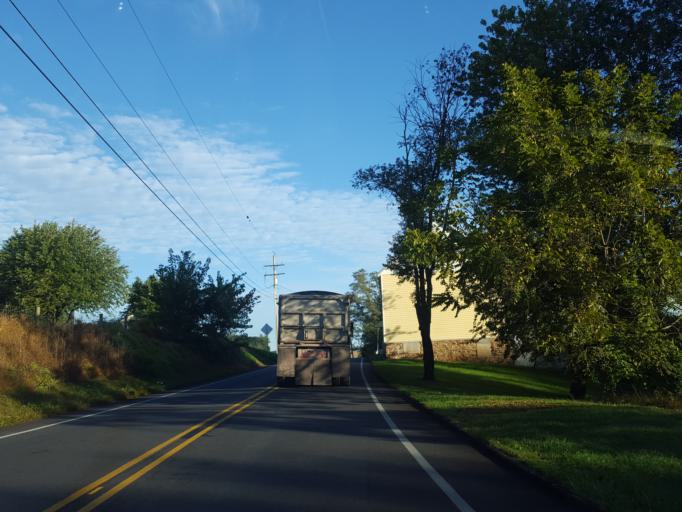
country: US
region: Pennsylvania
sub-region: York County
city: Stonybrook
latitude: 39.9567
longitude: -76.6089
